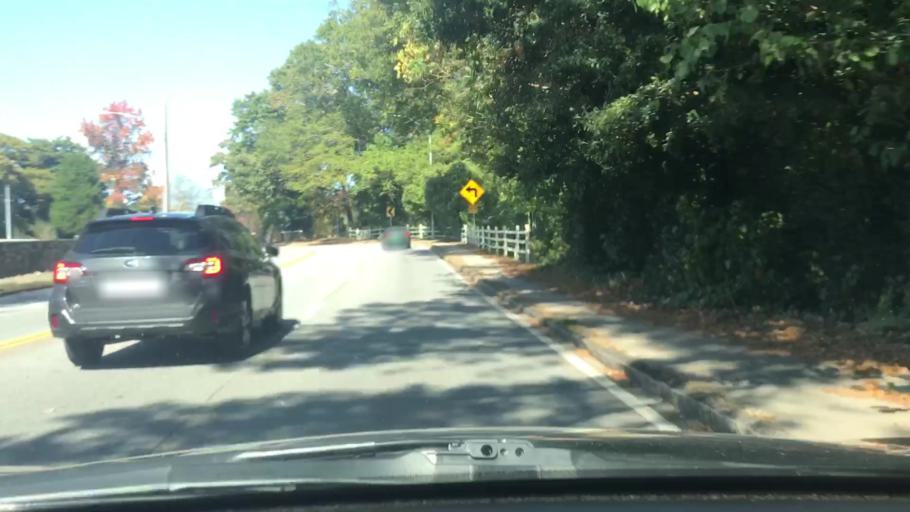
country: US
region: Georgia
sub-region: DeKalb County
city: Decatur
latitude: 33.7770
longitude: -84.2917
